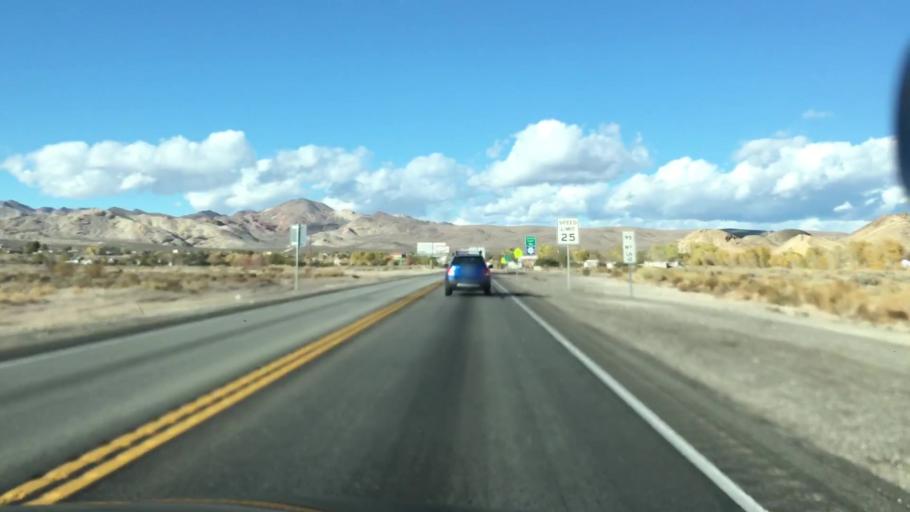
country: US
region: Nevada
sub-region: Nye County
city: Beatty
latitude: 36.8986
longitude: -116.7535
